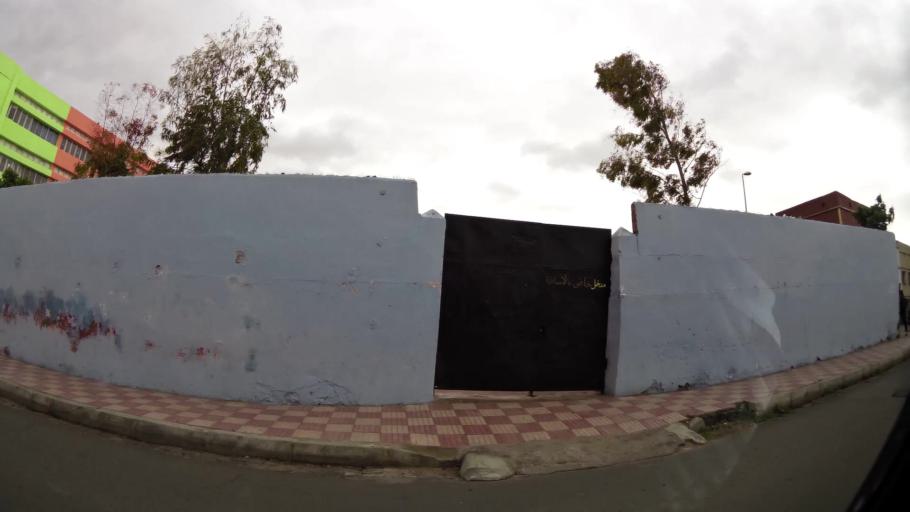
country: MA
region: Grand Casablanca
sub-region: Casablanca
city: Casablanca
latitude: 33.5854
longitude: -7.5598
